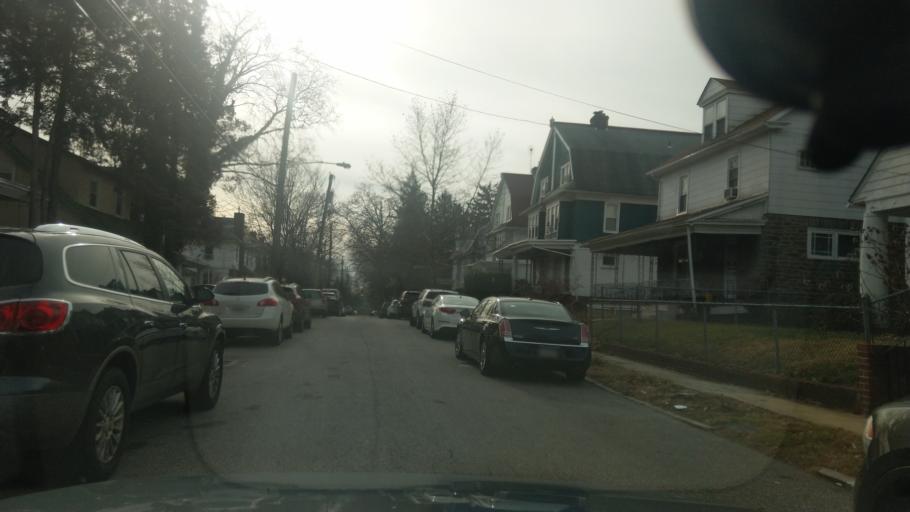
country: US
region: Pennsylvania
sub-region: Montgomery County
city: Wyncote
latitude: 40.0511
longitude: -75.1391
